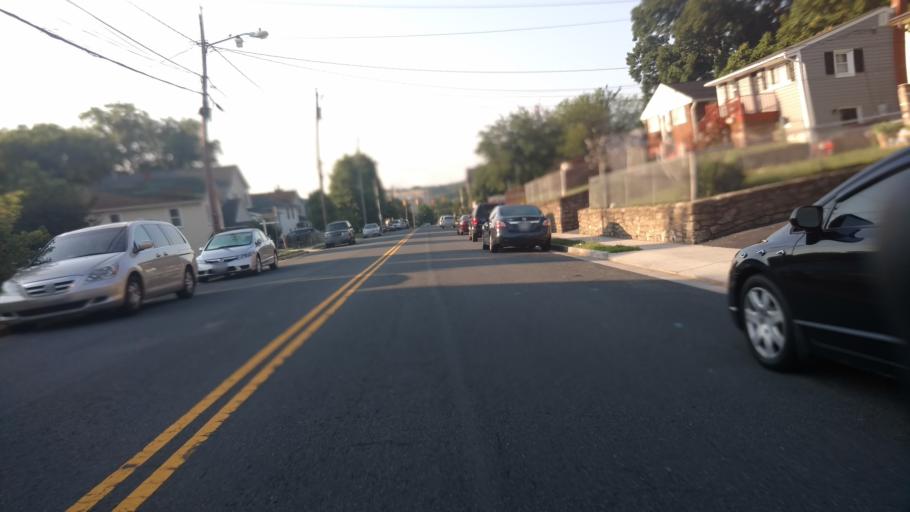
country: US
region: Virginia
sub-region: Arlington County
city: Arlington
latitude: 38.8512
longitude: -77.0865
